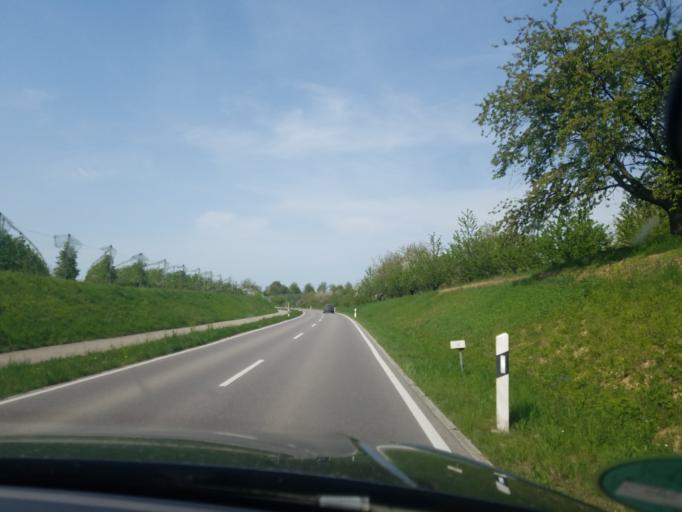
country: DE
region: Baden-Wuerttemberg
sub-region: Freiburg Region
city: Haslach
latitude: 48.5683
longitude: 8.0548
